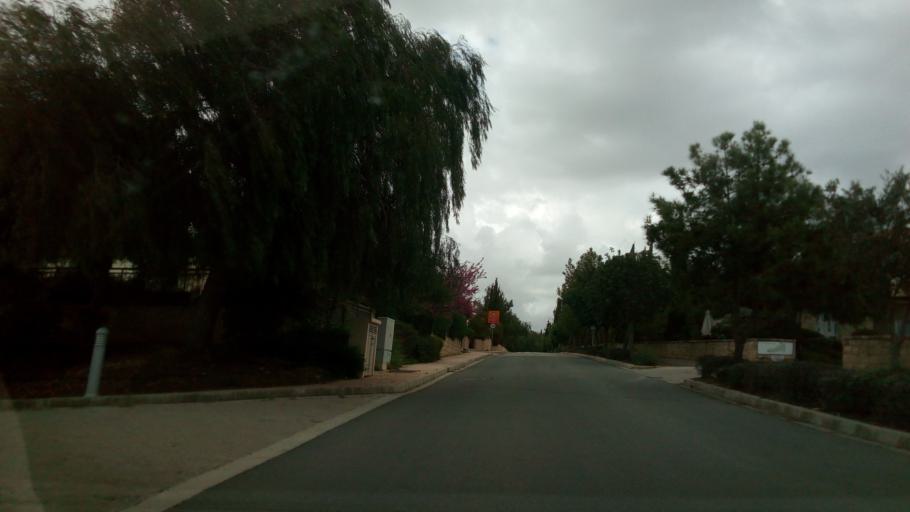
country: CY
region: Limassol
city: Pissouri
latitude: 34.6827
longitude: 32.6092
